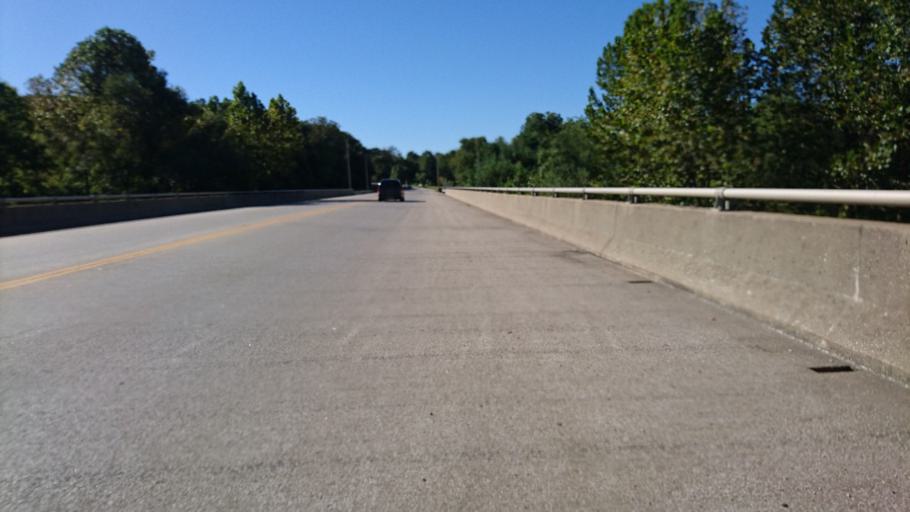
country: US
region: Missouri
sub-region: Jasper County
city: Joplin
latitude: 37.1014
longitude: -94.4949
